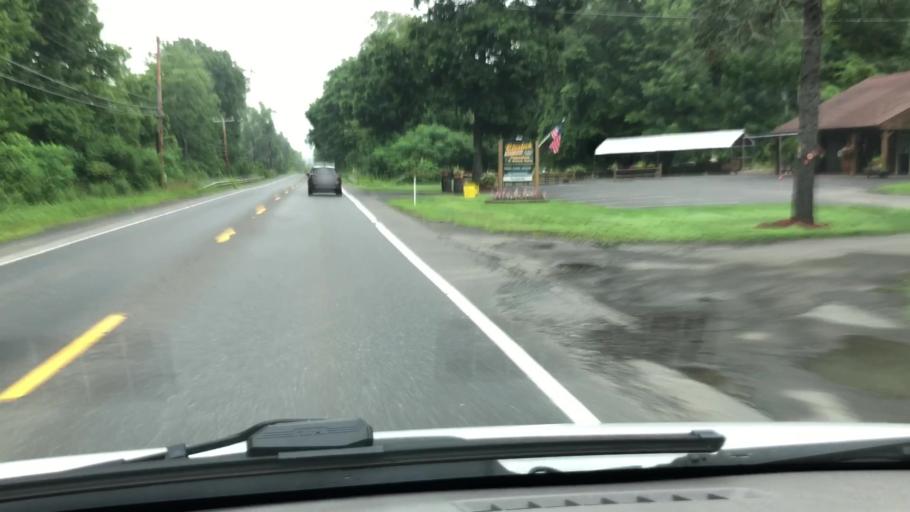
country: US
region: Massachusetts
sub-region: Franklin County
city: Greenfield
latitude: 42.5460
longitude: -72.6012
